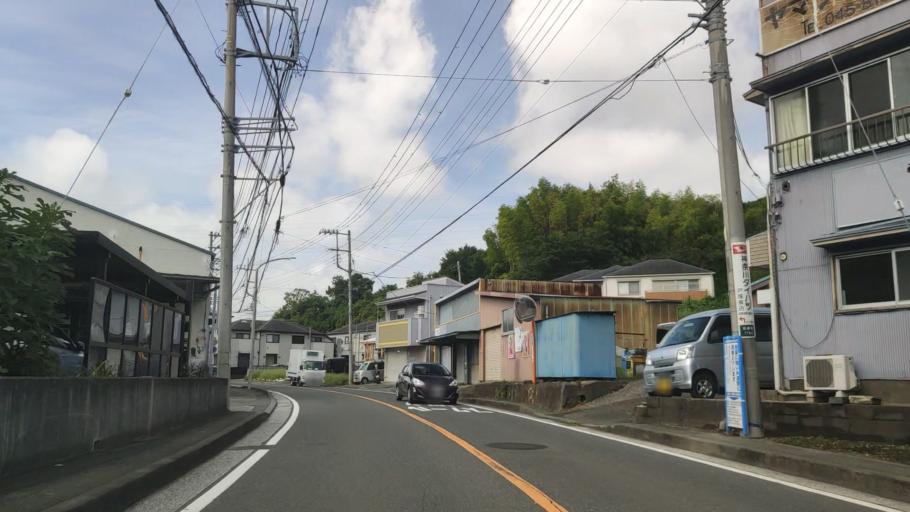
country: JP
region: Kanagawa
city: Minami-rinkan
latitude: 35.4312
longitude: 139.5353
